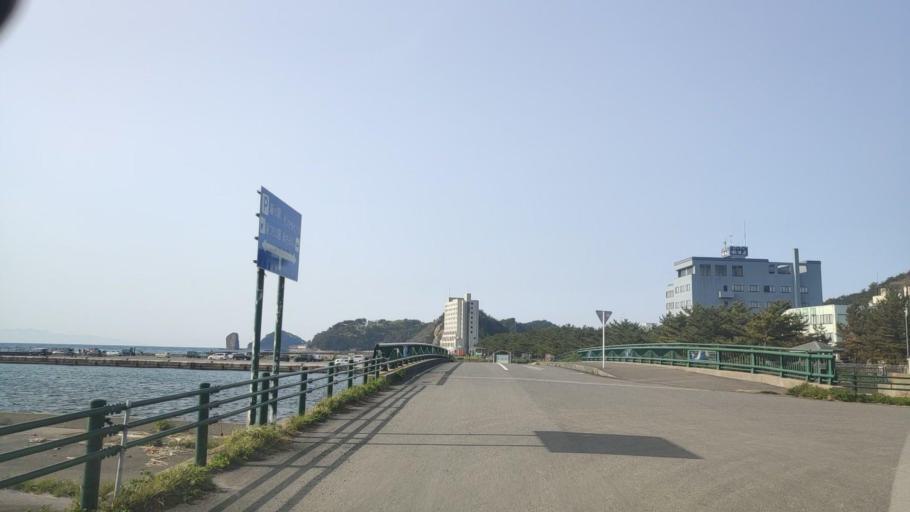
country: JP
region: Aomori
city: Aomori Shi
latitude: 40.8924
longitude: 140.8606
